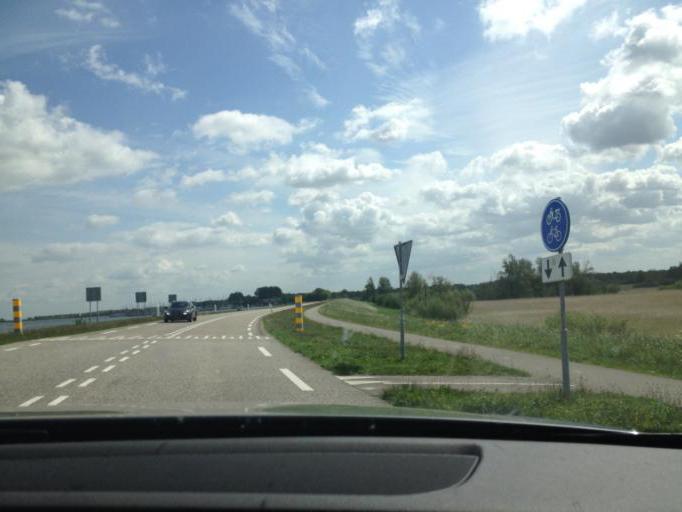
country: NL
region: Flevoland
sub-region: Gemeente Almere
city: Almere Stad
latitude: 52.4160
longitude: 5.2074
